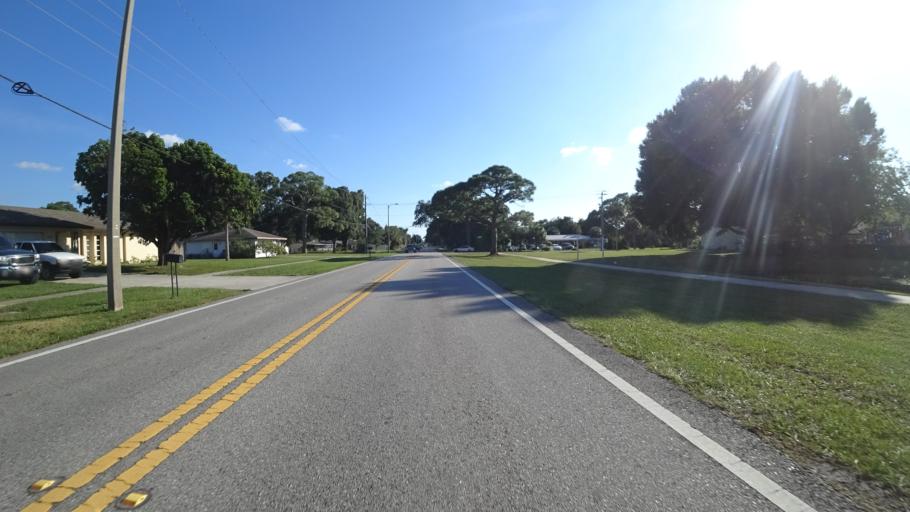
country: US
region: Florida
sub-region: Manatee County
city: West Bradenton
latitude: 27.4782
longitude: -82.6041
